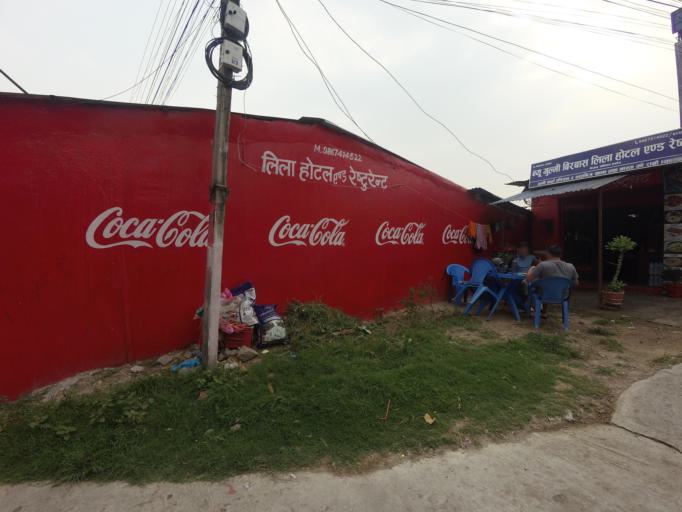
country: NP
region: Western Region
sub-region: Lumbini Zone
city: Bhairahawa
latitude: 27.4900
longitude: 83.4494
